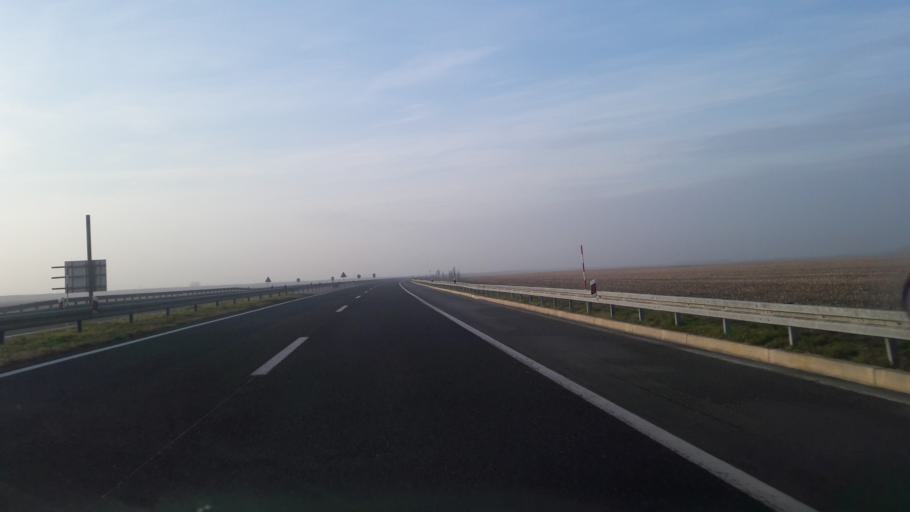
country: HR
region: Osjecko-Baranjska
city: Josipovac
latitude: 45.5640
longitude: 18.5473
